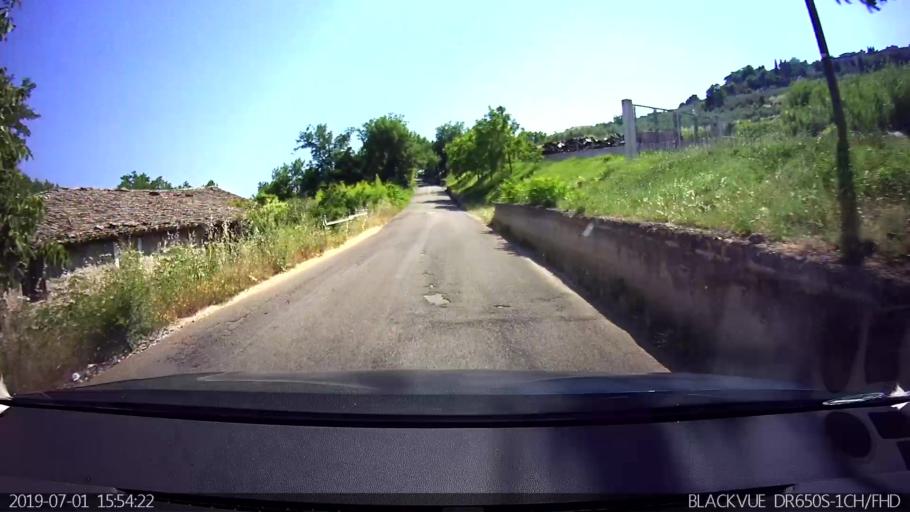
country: IT
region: Latium
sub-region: Provincia di Frosinone
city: Veroli
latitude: 41.6948
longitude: 13.4275
